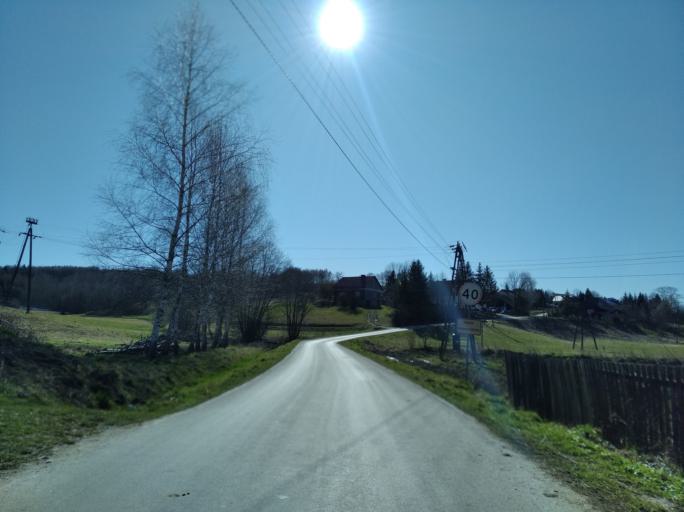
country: PL
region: Subcarpathian Voivodeship
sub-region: Powiat strzyzowski
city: Wisniowa
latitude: 49.9131
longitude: 21.7089
